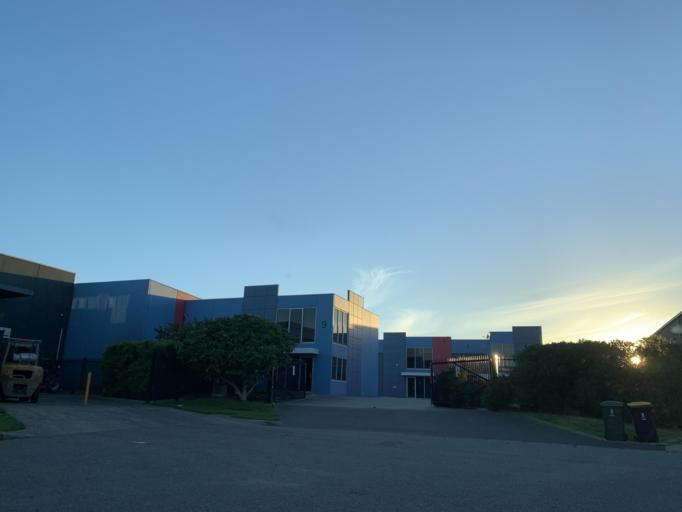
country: AU
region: Victoria
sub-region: Kingston
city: Aspendale Gardens
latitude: -38.0089
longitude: 145.1068
